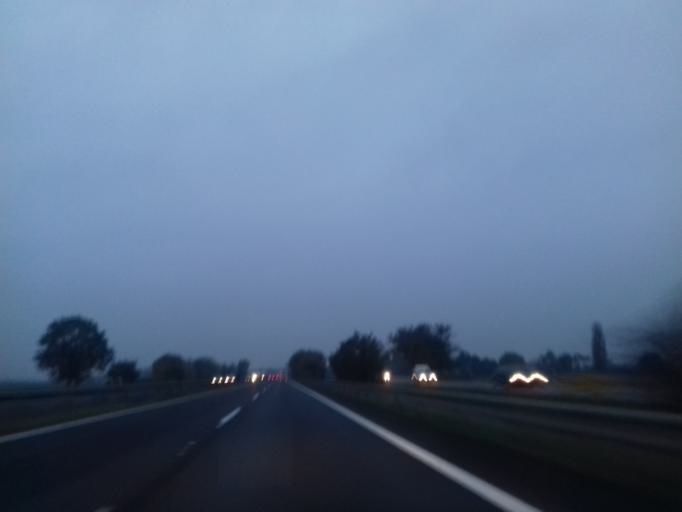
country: CZ
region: Olomoucky
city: Naklo
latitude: 49.6578
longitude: 17.1117
